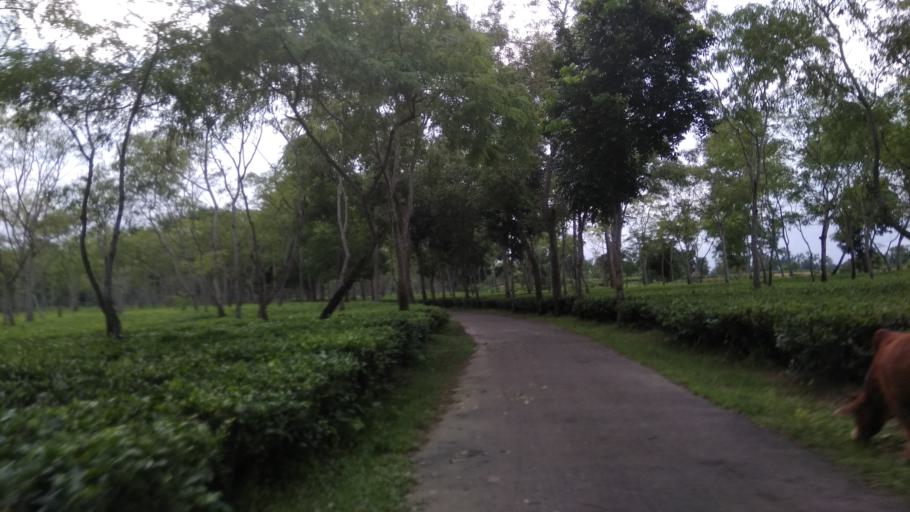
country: IN
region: Tripura
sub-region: Dhalai
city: Kamalpur
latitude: 24.1768
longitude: 91.8774
